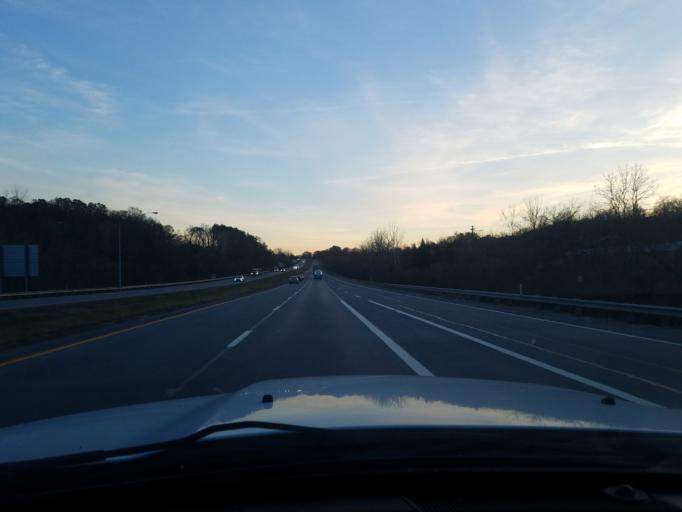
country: US
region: West Virginia
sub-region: Wood County
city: Williamstown
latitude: 39.3867
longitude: -81.4398
